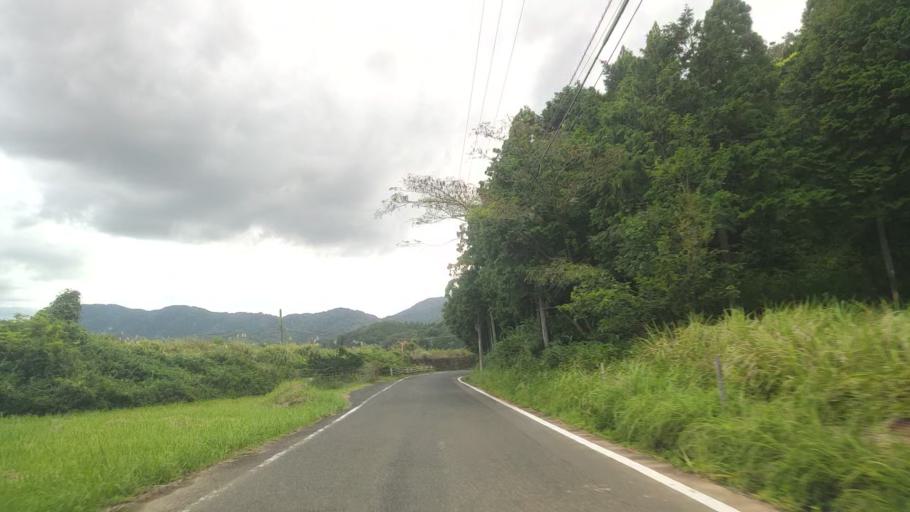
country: JP
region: Hyogo
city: Toyooka
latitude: 35.6004
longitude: 134.8879
